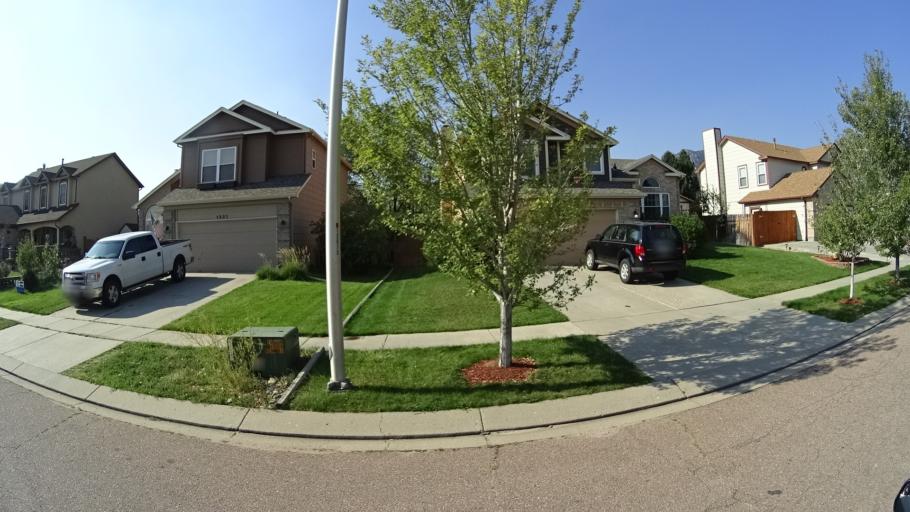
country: US
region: Colorado
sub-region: El Paso County
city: Stratmoor
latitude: 38.7716
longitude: -104.8045
